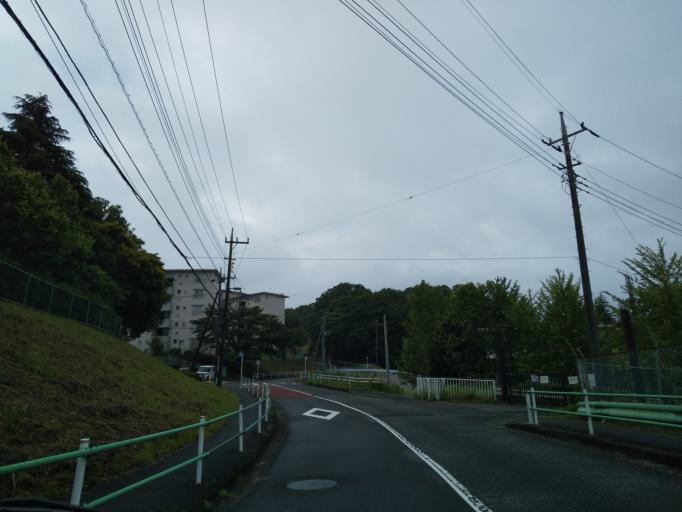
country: JP
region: Tokyo
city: Hino
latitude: 35.6519
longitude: 139.4104
